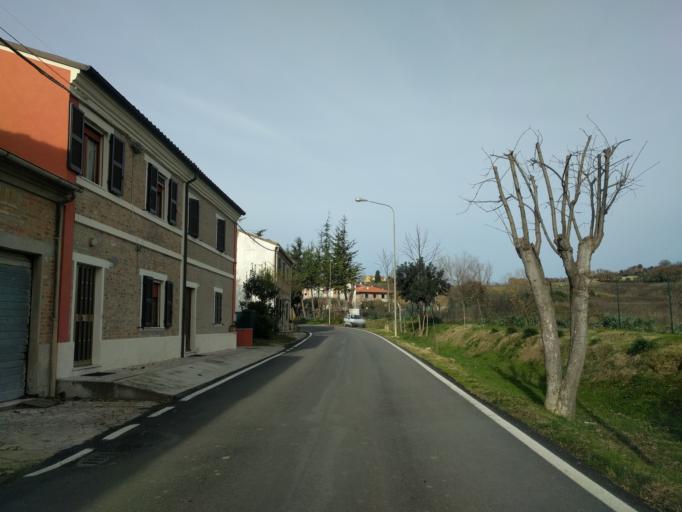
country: IT
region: The Marches
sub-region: Provincia di Pesaro e Urbino
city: Cuccurano
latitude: 43.7949
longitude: 12.9530
